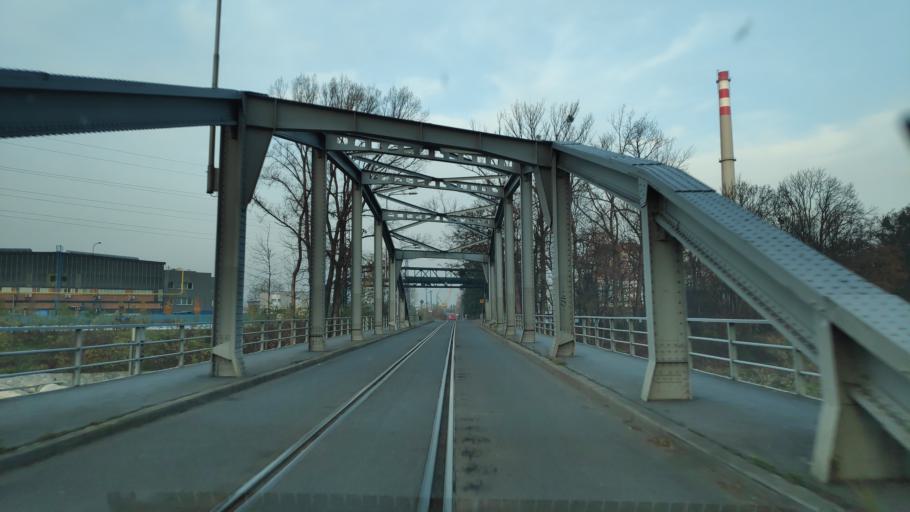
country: CZ
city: Sviadnov
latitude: 49.6965
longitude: 18.3279
